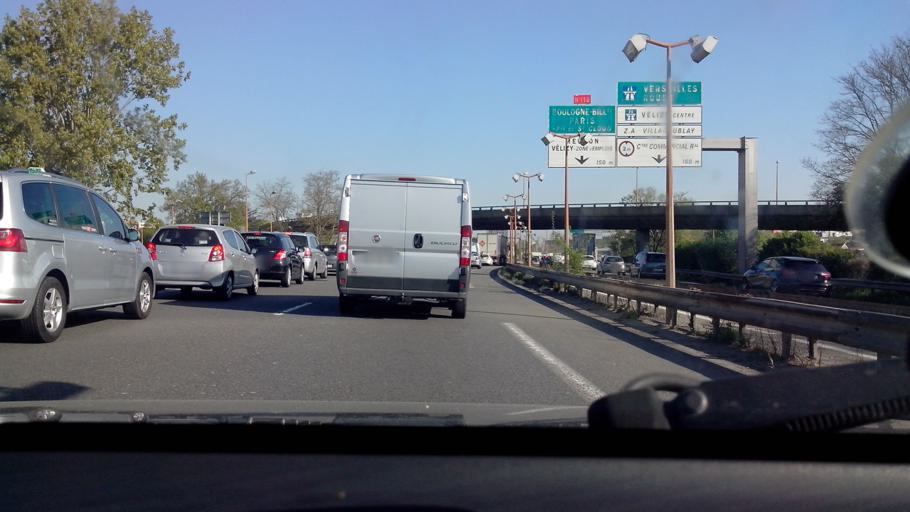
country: FR
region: Ile-de-France
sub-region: Departement de l'Essonne
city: Bievres
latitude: 48.7760
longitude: 2.2224
